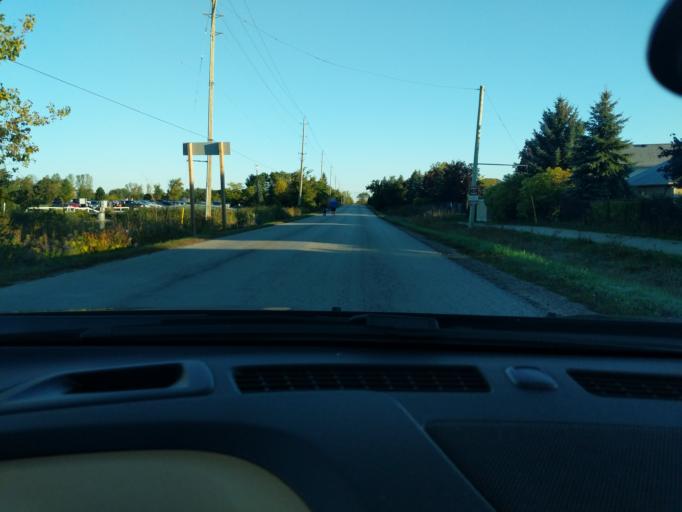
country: CA
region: Ontario
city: Collingwood
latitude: 44.4896
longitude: -80.2485
